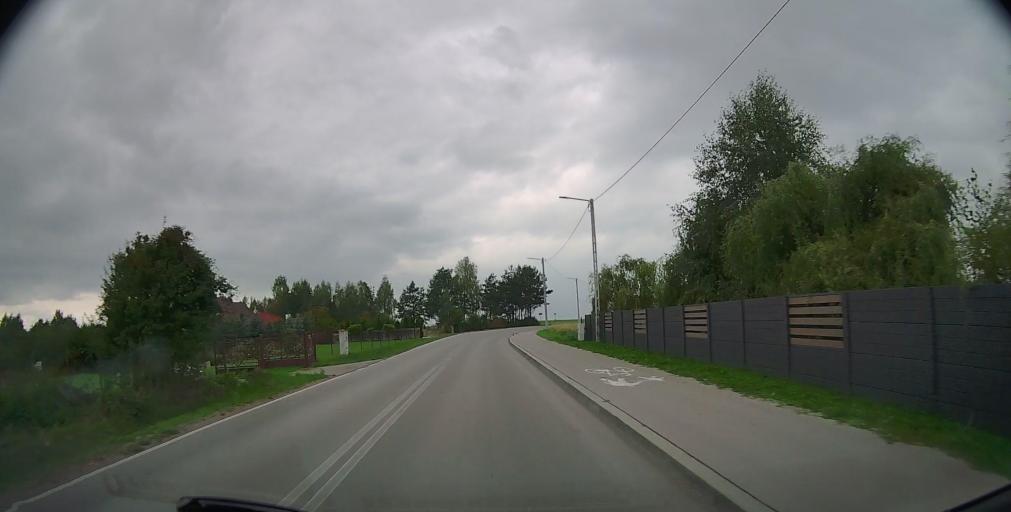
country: PL
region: Masovian Voivodeship
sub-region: Powiat radomski
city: Zakrzew
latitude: 51.4355
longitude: 21.0517
